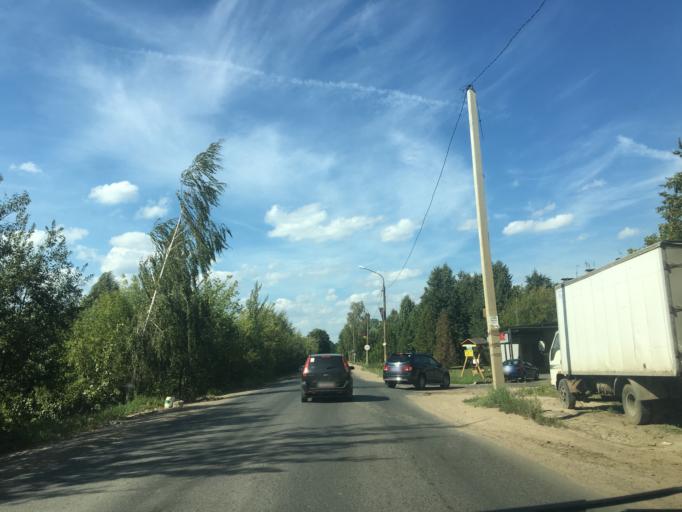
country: RU
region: Moskovskaya
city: Vidnoye
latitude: 55.5142
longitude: 37.6842
